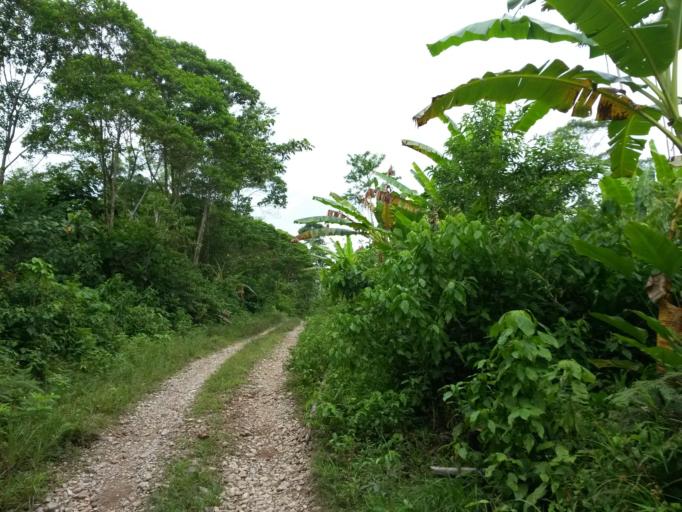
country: CO
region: Putumayo
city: Puerto Guzman
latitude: 1.0190
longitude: -76.3686
